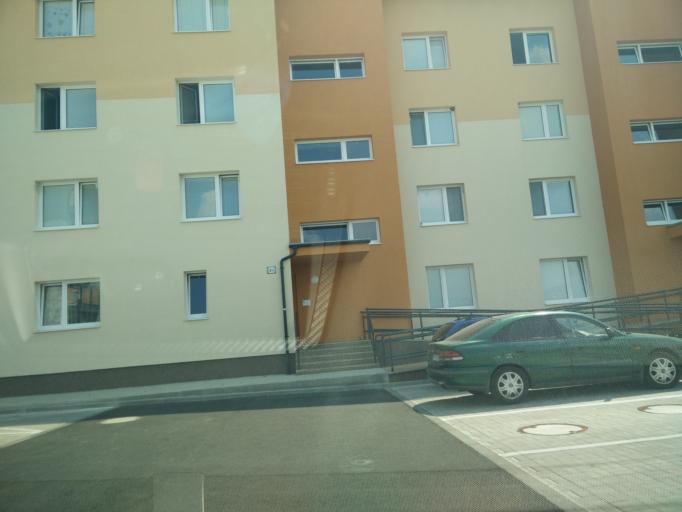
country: SK
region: Banskobystricky
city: Ziar nad Hronom
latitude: 48.6018
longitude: 18.8393
